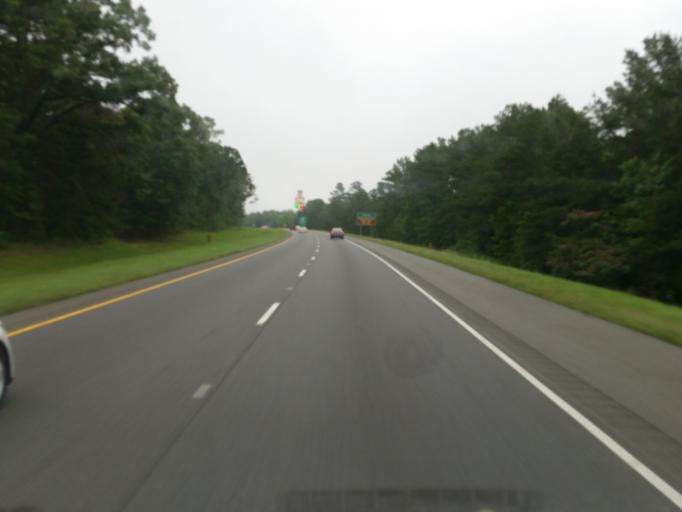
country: US
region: Louisiana
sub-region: Bossier Parish
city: Haughton
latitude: 32.5436
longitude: -93.5240
